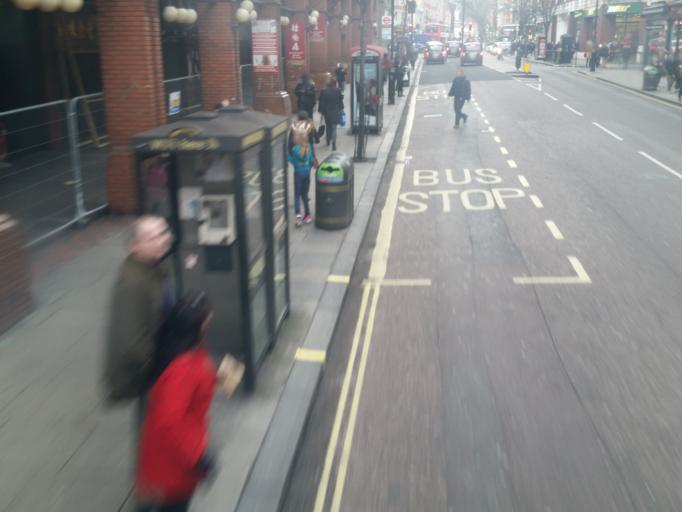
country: GB
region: England
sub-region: Greater London
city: London
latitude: 51.5123
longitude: -0.1285
